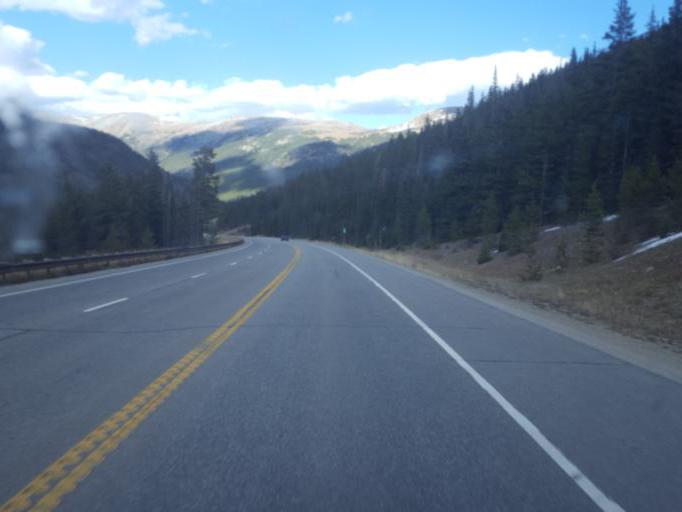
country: US
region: Colorado
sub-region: Summit County
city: Breckenridge
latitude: 39.4482
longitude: -106.1508
